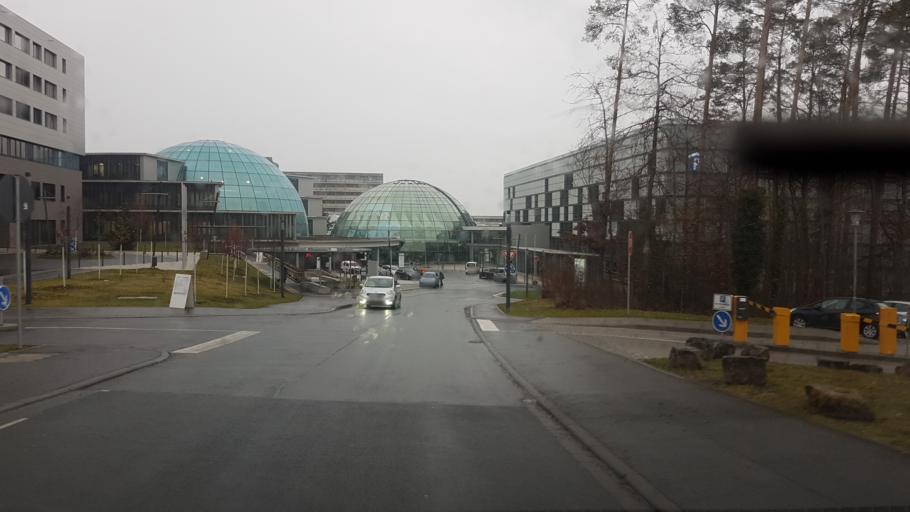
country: DE
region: Bavaria
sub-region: Regierungsbezirk Unterfranken
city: Salz
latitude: 50.3236
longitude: 10.2364
